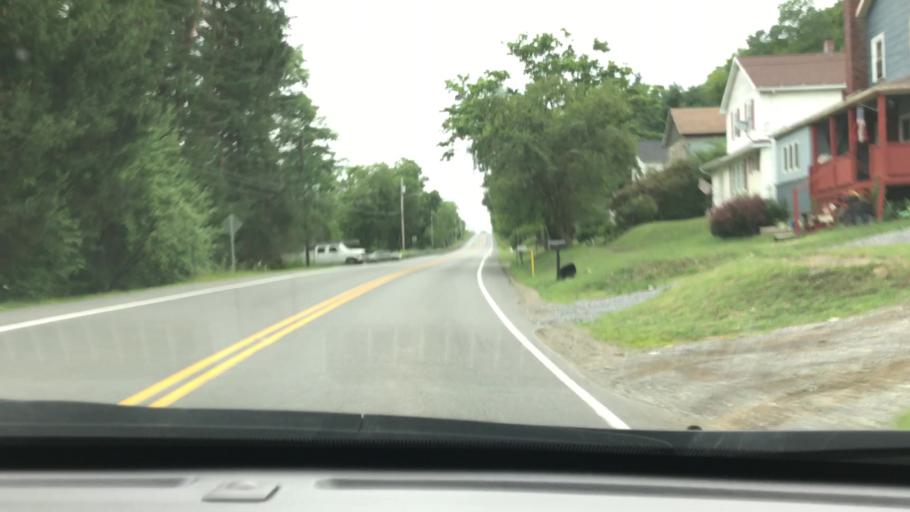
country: US
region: Pennsylvania
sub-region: Elk County
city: Johnsonburg
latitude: 41.5803
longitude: -78.6884
